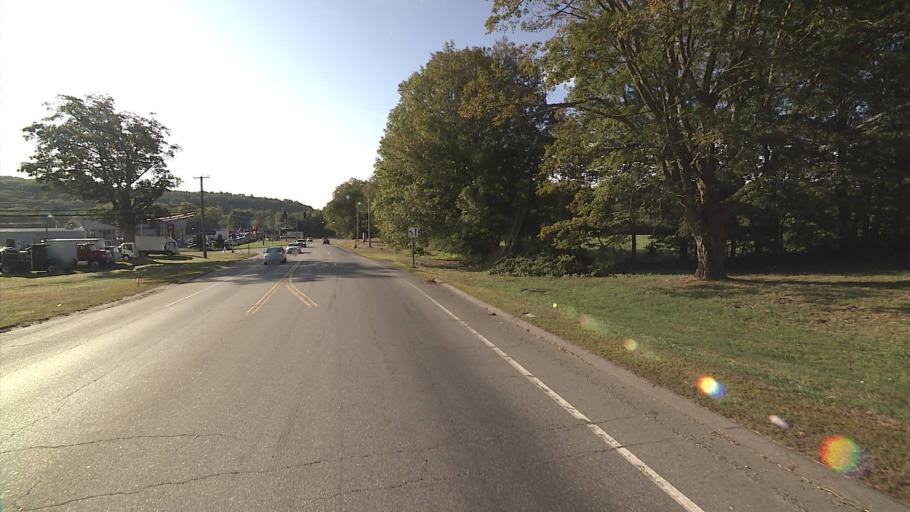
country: US
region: Connecticut
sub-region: New London County
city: Baltic
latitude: 41.5676
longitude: -72.1307
